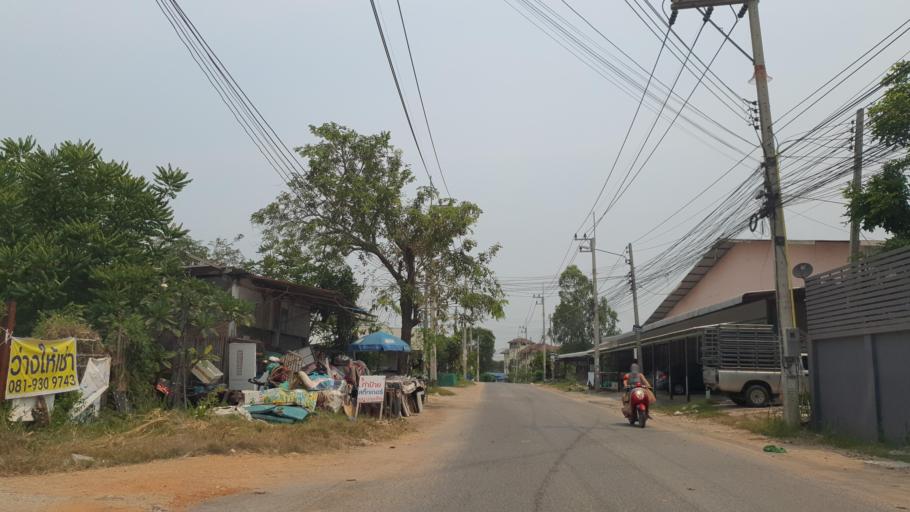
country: TH
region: Chon Buri
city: Phatthaya
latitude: 12.8965
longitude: 100.9065
